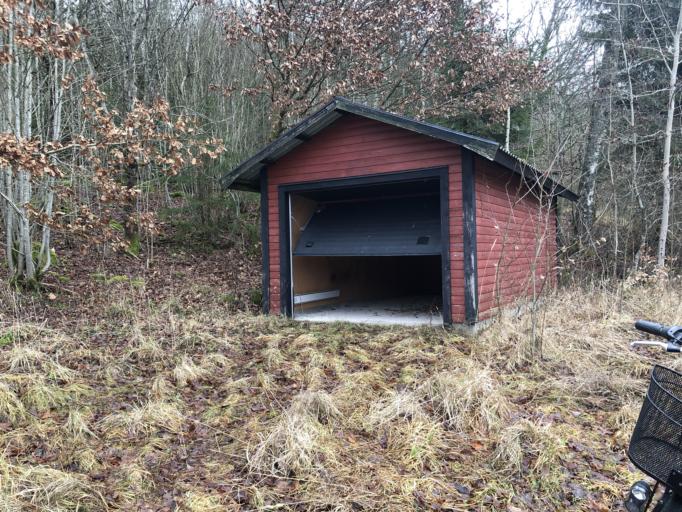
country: SE
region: Vaestra Goetaland
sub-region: Ulricehamns Kommun
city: Ulricehamn
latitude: 57.7898
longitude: 13.3919
